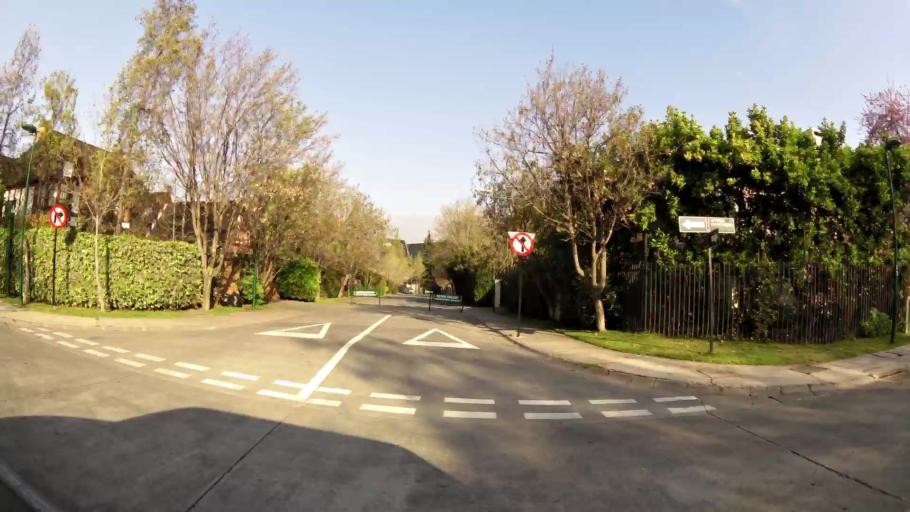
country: CL
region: Santiago Metropolitan
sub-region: Provincia de Santiago
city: Villa Presidente Frei, Nunoa, Santiago, Chile
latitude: -33.3542
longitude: -70.5374
